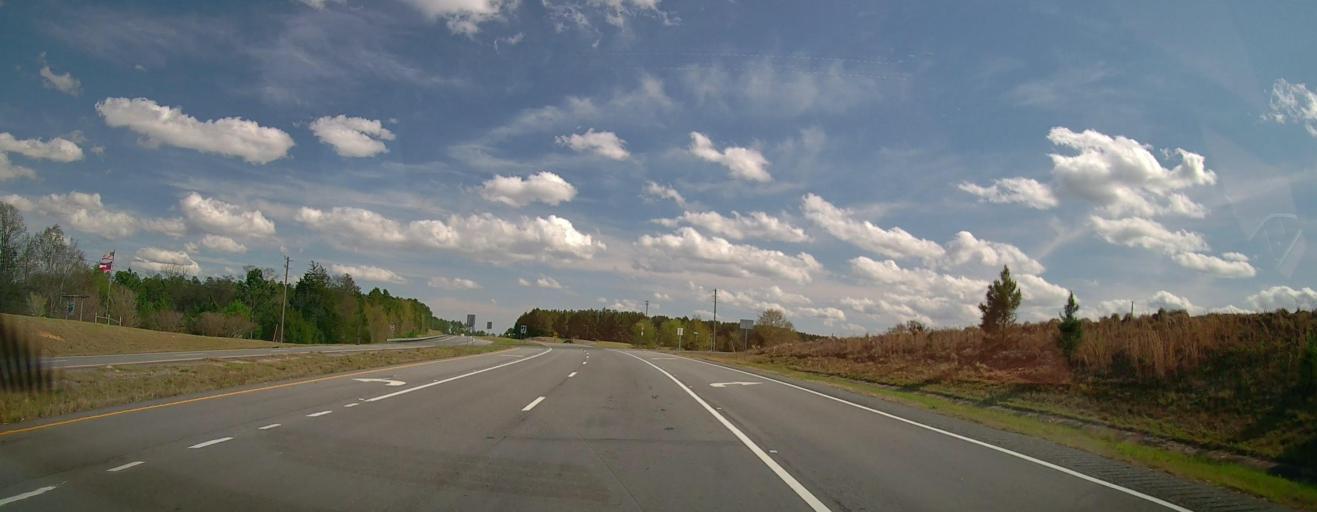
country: US
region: Georgia
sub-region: Baldwin County
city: Hardwick
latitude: 33.0028
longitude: -83.2203
